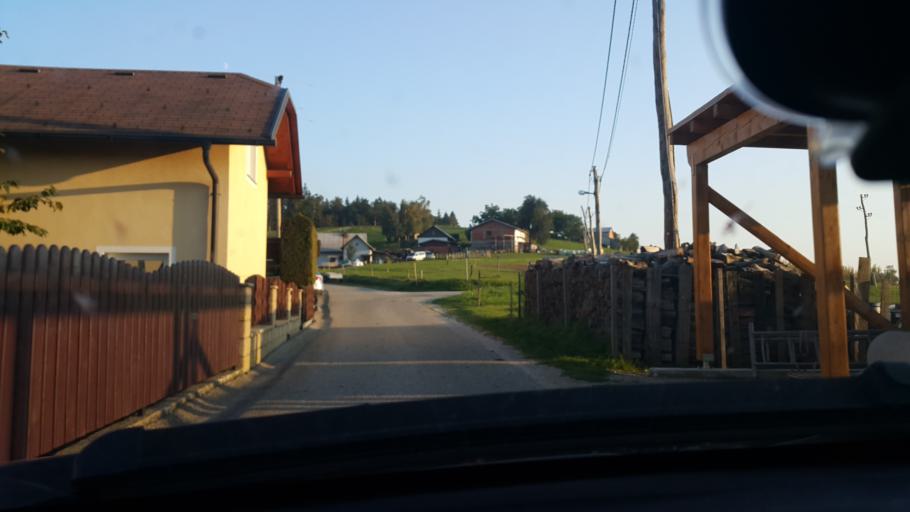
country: SI
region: Race-Fram
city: Morje
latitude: 46.4559
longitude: 15.6014
